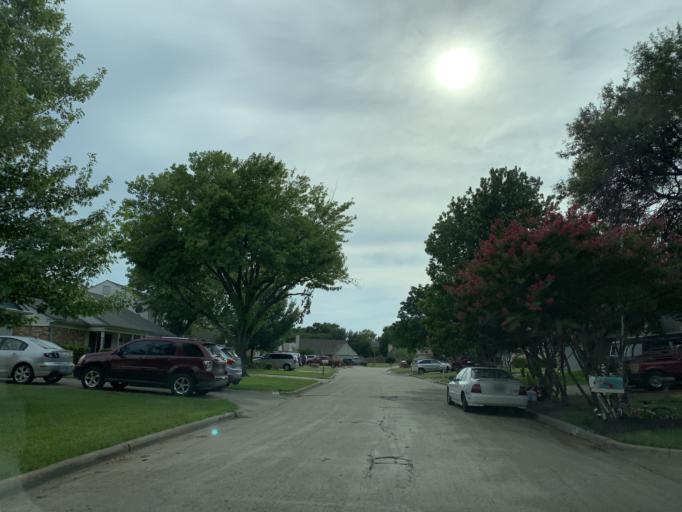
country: US
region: Texas
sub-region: Dallas County
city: Grand Prairie
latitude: 32.6686
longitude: -97.0453
